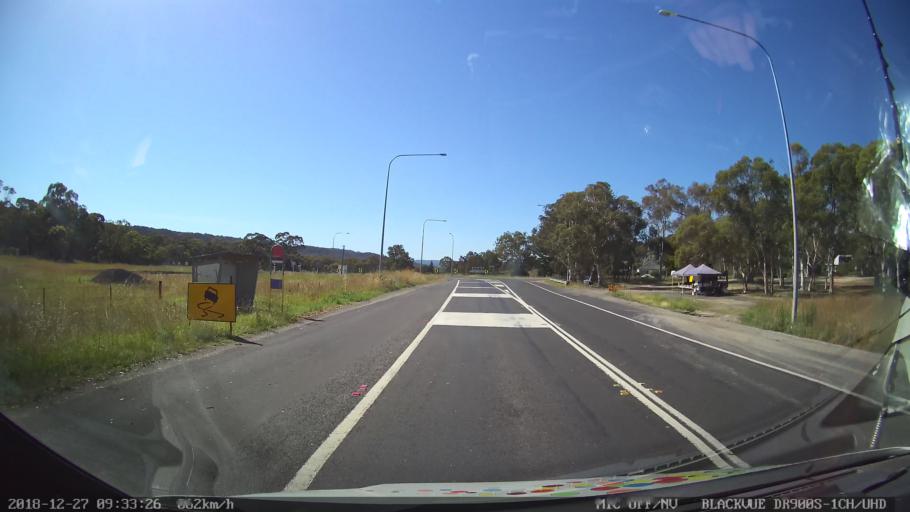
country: AU
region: New South Wales
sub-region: Lithgow
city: Portland
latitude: -33.2185
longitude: 150.0216
